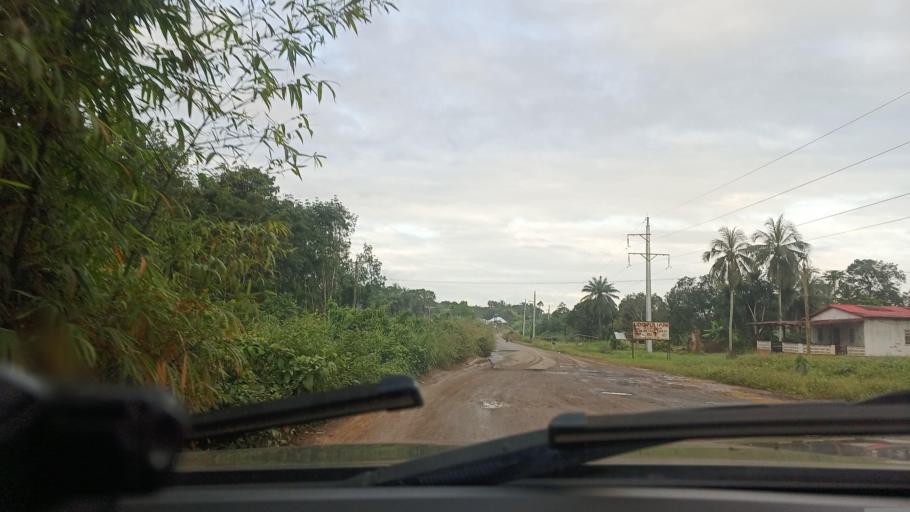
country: LR
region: Montserrado
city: Monrovia
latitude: 6.5608
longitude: -10.8706
